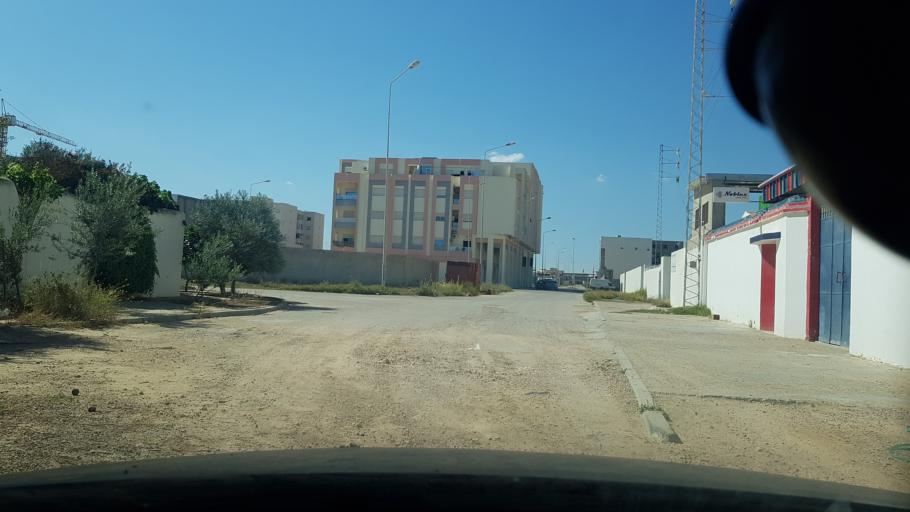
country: TN
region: Safaqis
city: Al Qarmadah
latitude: 34.8326
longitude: 10.7612
